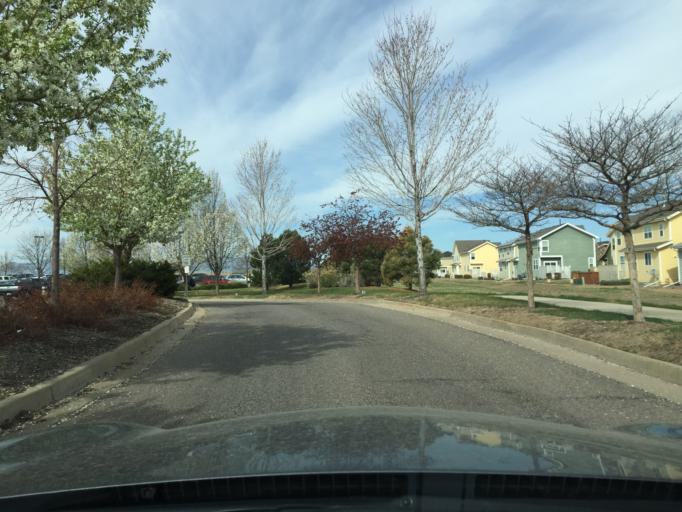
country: US
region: Colorado
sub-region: Broomfield County
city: Broomfield
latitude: 39.9358
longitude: -105.0349
